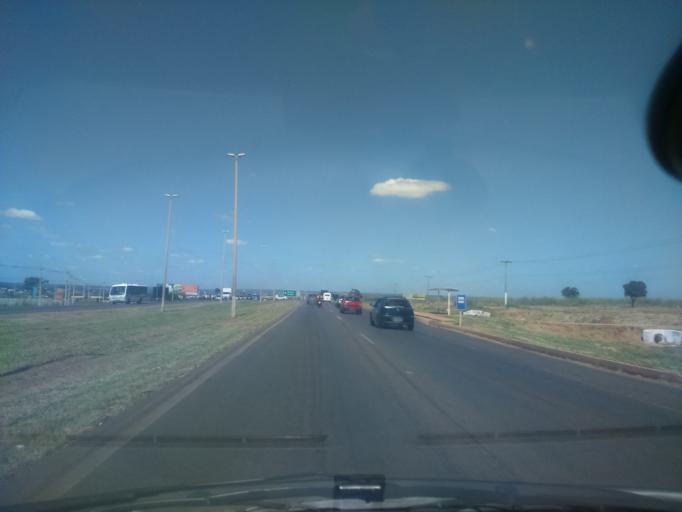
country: BR
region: Goias
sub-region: Luziania
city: Luziania
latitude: -16.0958
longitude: -47.9806
